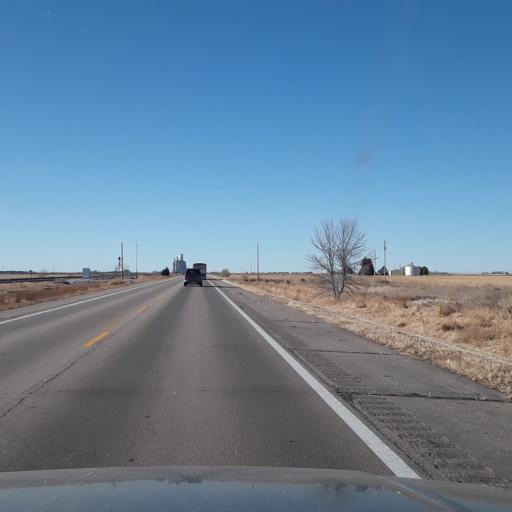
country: US
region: Nebraska
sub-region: Kearney County
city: Minden
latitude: 40.4958
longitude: -99.0010
